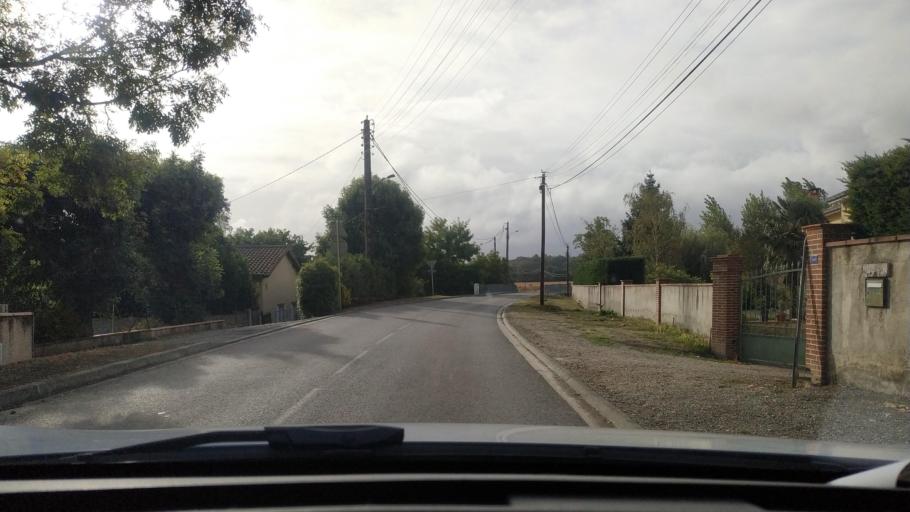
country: FR
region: Midi-Pyrenees
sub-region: Departement de la Haute-Garonne
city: Gaillac-Toulza
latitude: 43.2979
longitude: 1.4708
